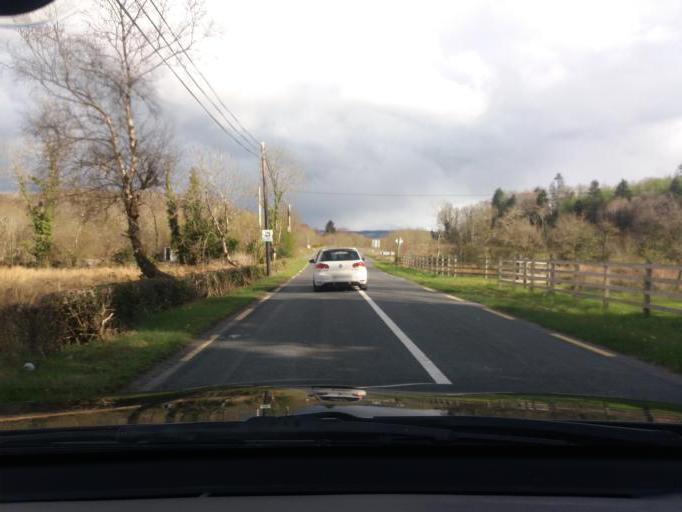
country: IE
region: Connaught
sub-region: County Leitrim
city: Manorhamilton
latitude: 54.3290
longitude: -8.2095
